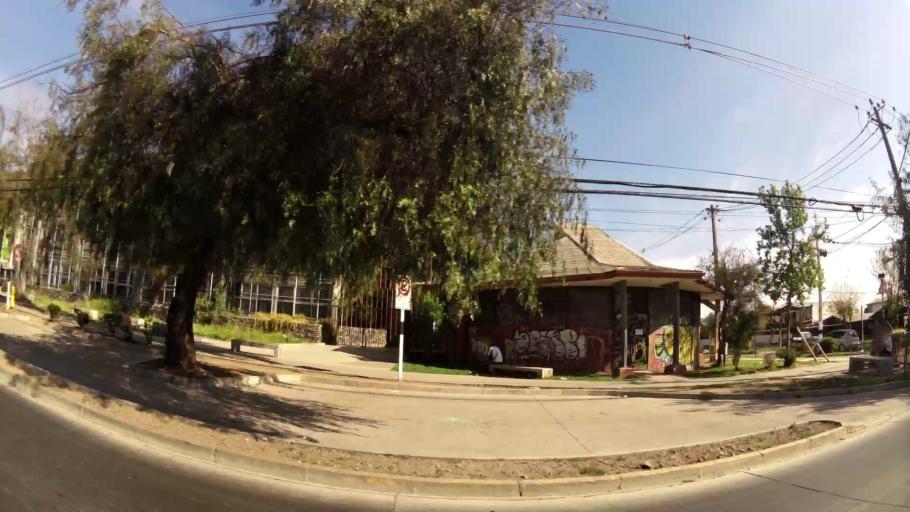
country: CL
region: Santiago Metropolitan
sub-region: Provincia de Santiago
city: Villa Presidente Frei, Nunoa, Santiago, Chile
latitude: -33.4702
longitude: -70.5724
